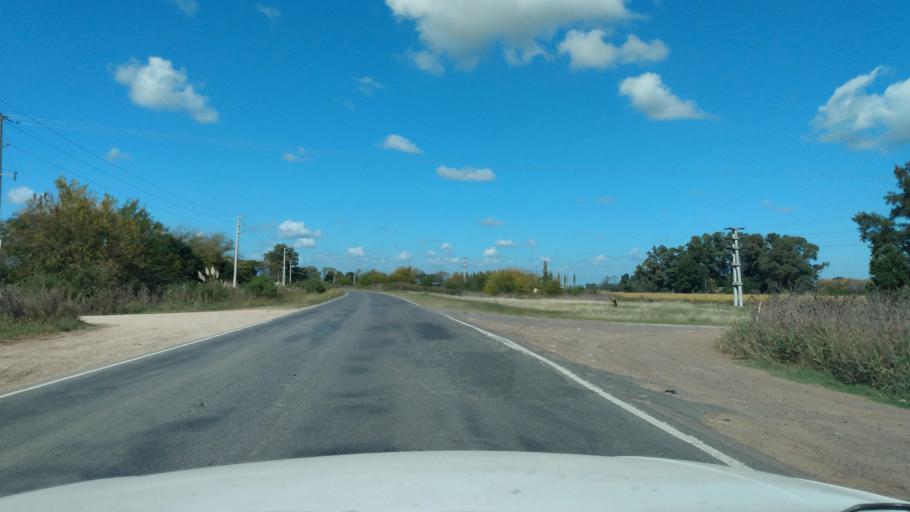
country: AR
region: Buenos Aires
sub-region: Partido de Mercedes
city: Mercedes
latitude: -34.7018
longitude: -59.4030
